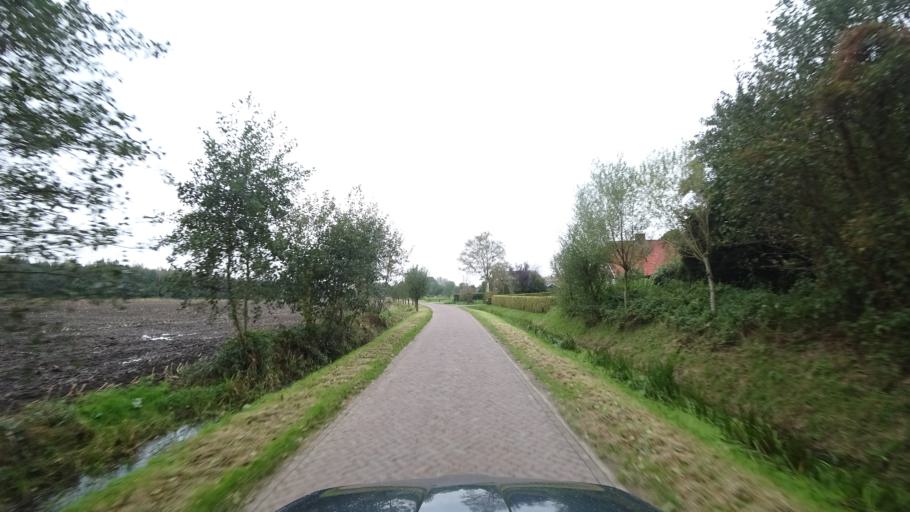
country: NL
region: Gelderland
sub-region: Gemeente Nijkerk
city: Nijkerk
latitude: 52.2393
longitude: 5.5081
